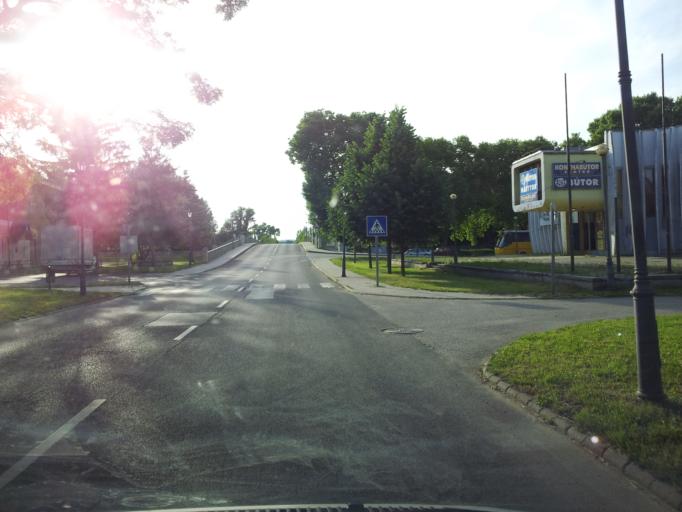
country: HU
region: Komarom-Esztergom
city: Esztergom
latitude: 47.7870
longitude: 18.7360
